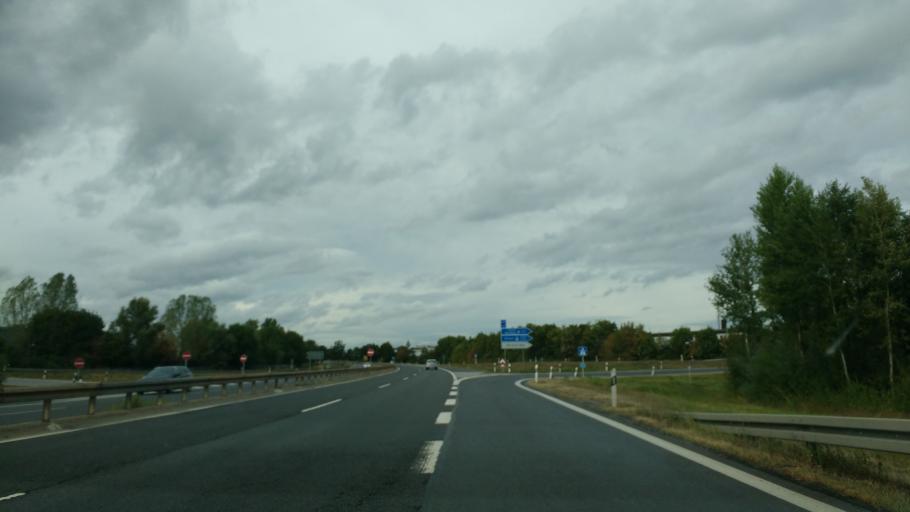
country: DE
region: Bavaria
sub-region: Regierungsbezirk Unterfranken
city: Sennfeld
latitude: 50.0247
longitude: 10.2380
